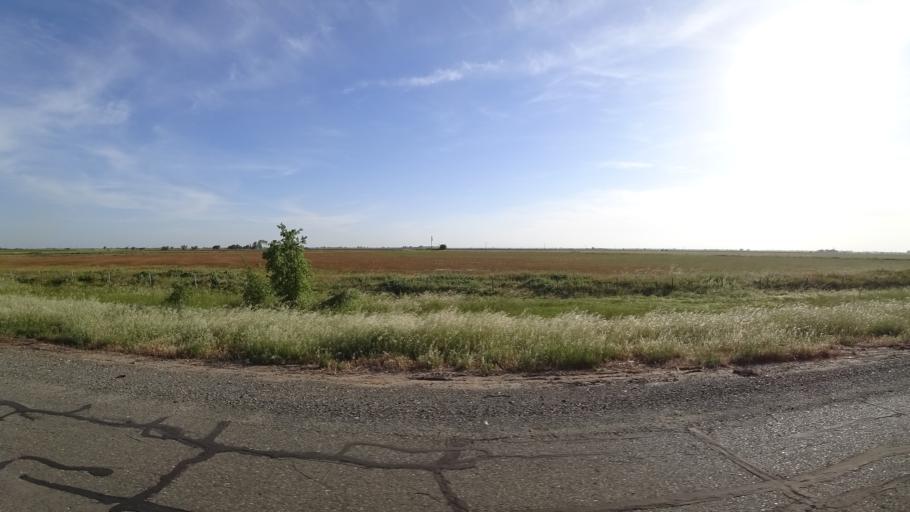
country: US
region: California
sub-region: Yuba County
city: Plumas Lake
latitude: 39.0514
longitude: -121.4946
